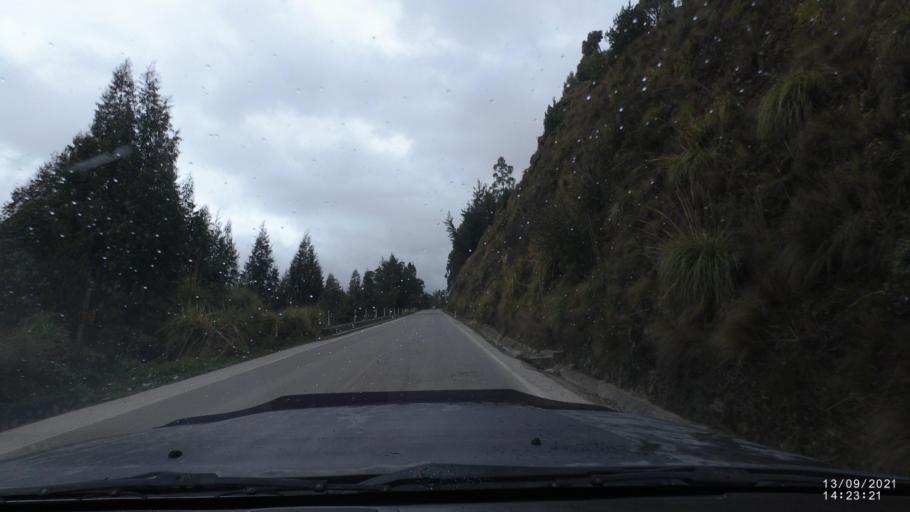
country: BO
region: Cochabamba
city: Colomi
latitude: -17.2742
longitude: -65.8758
